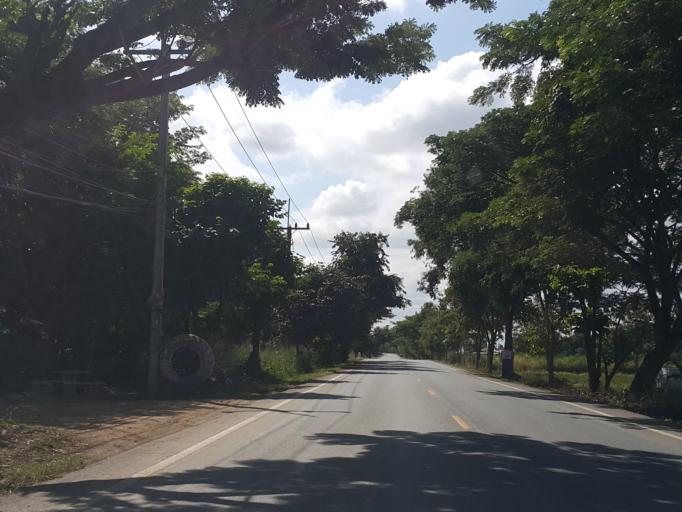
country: TH
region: Lamphun
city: Ban Thi
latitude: 18.6830
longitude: 99.1522
